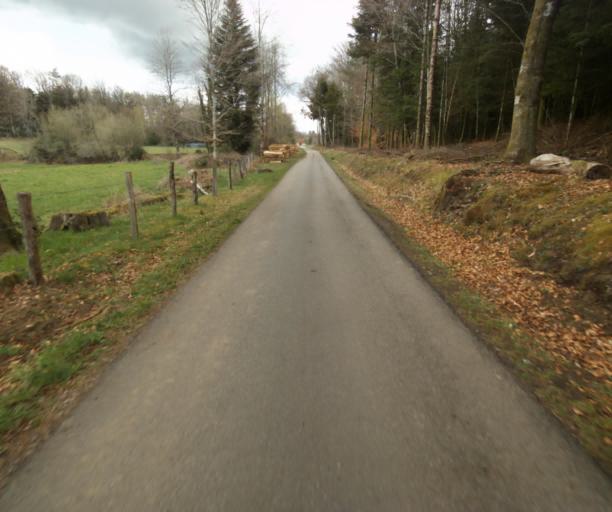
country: FR
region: Limousin
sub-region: Departement de la Correze
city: Correze
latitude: 45.2602
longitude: 1.9031
